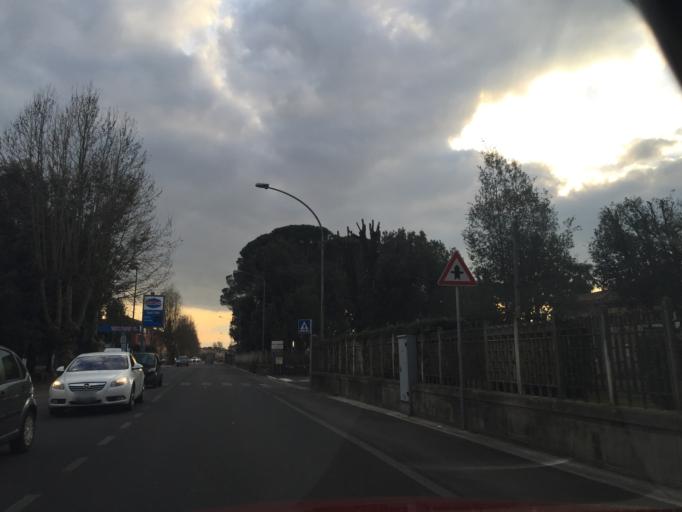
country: IT
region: Tuscany
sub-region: Provincia di Pistoia
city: Margine Coperta-Traversagna
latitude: 43.8840
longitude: 10.7495
